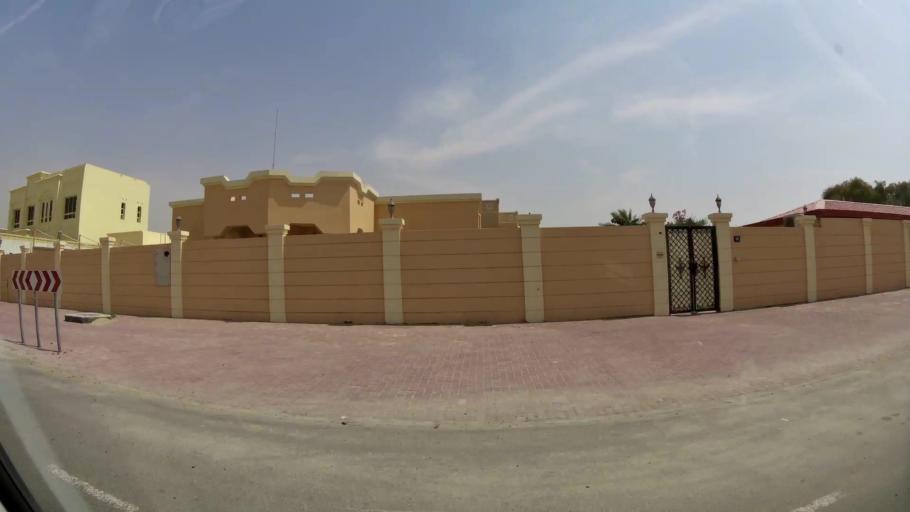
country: AE
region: Ash Shariqah
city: Sharjah
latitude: 25.2557
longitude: 55.4727
